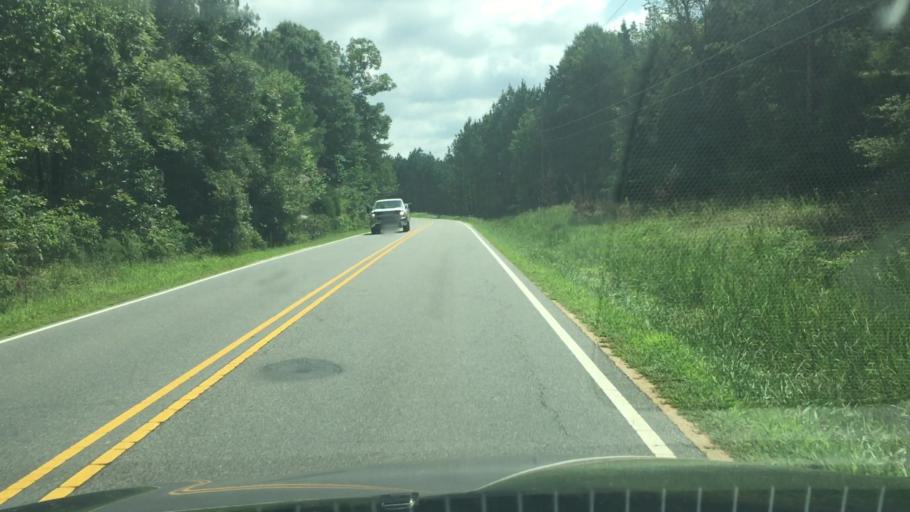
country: US
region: North Carolina
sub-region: Rowan County
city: Enochville
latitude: 35.4863
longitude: -80.7487
